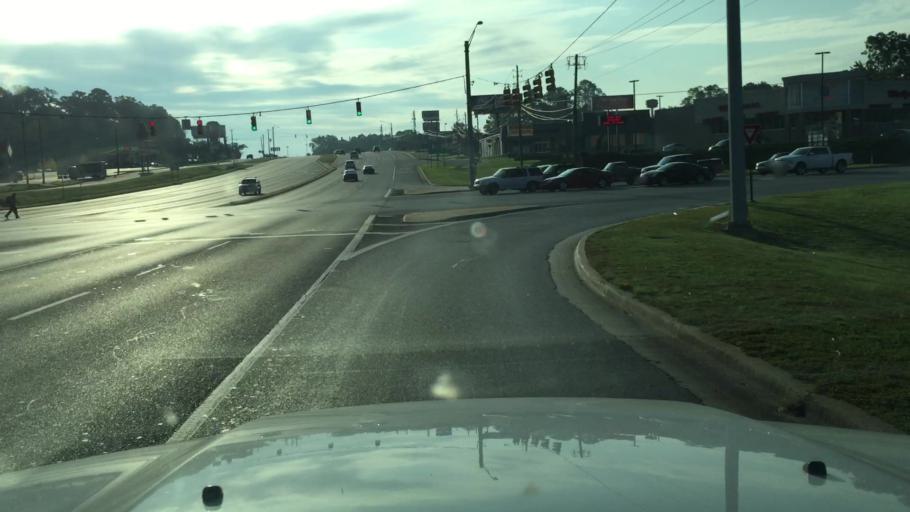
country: US
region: Alabama
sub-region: Tuscaloosa County
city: Northport
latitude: 33.2390
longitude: -87.5771
